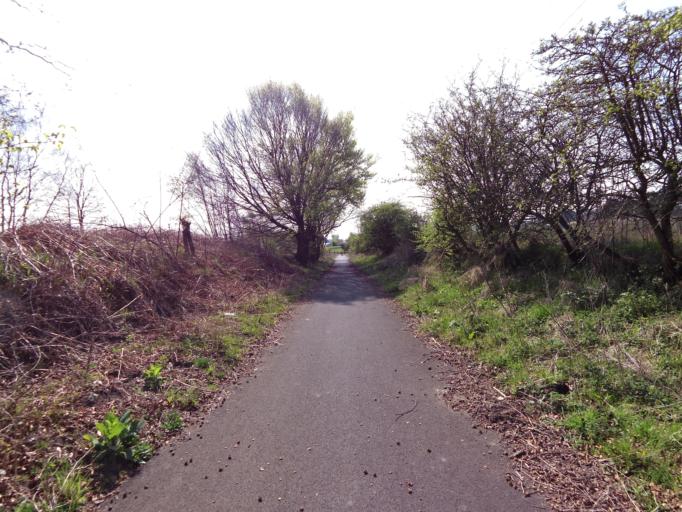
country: GB
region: Scotland
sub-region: Fife
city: Kirkcaldy
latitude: 56.1396
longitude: -3.1510
